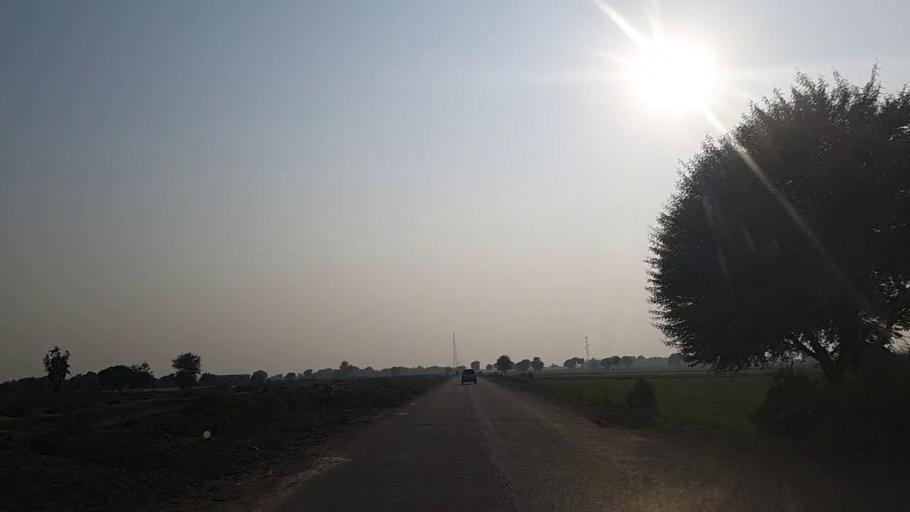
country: PK
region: Sindh
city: Shahpur Chakar
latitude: 26.2070
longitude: 68.5618
